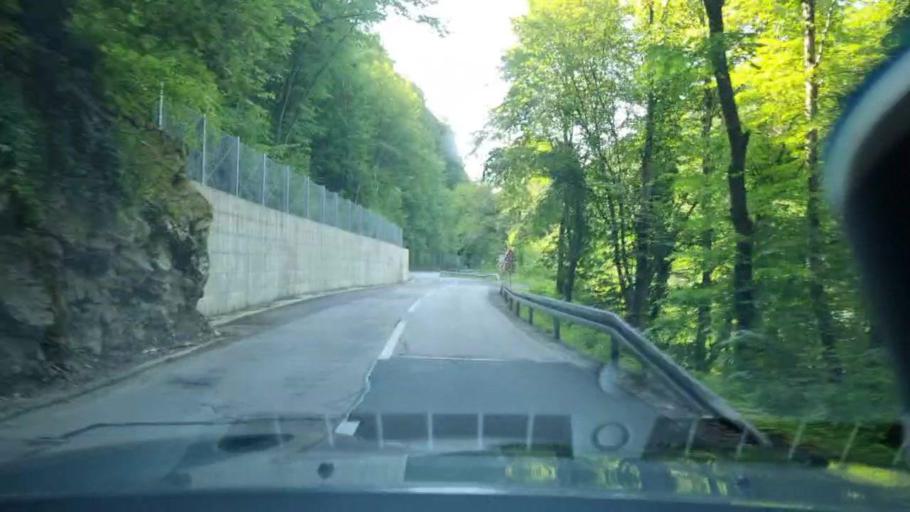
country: BA
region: Federation of Bosnia and Herzegovina
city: Stijena
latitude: 44.8880
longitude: 16.0557
